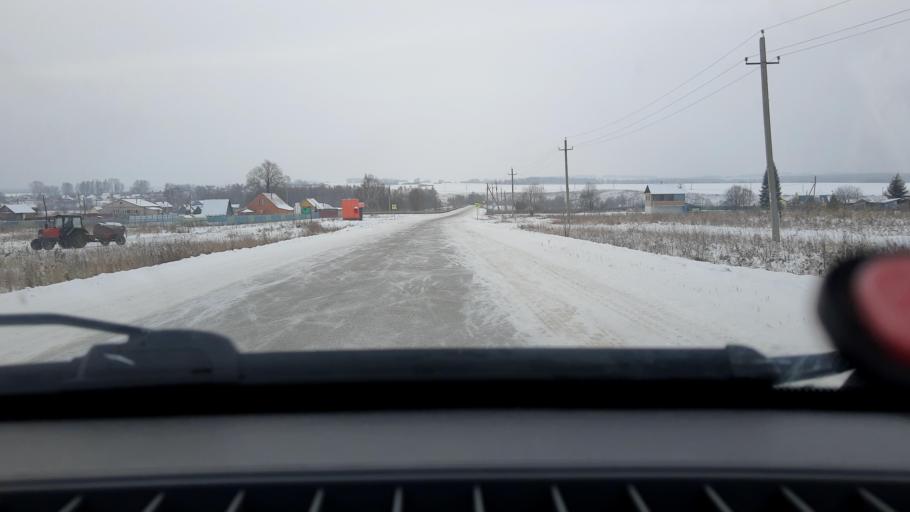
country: RU
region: Bashkortostan
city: Iglino
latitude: 54.6456
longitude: 56.4254
